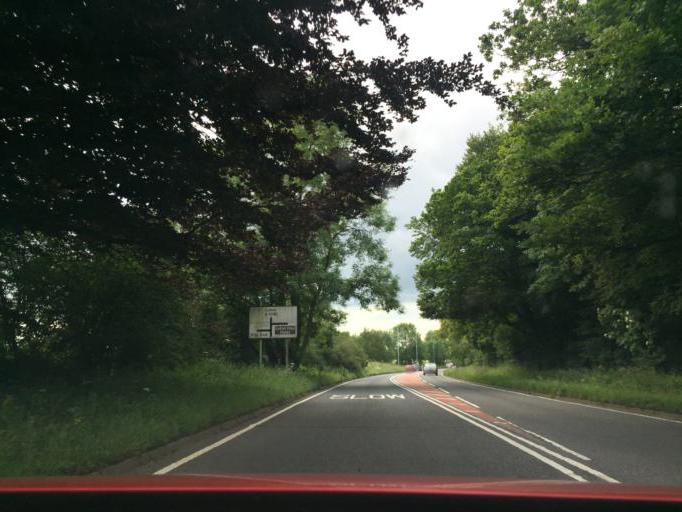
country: GB
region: England
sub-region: Luton
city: Luton
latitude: 51.8447
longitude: -0.4110
